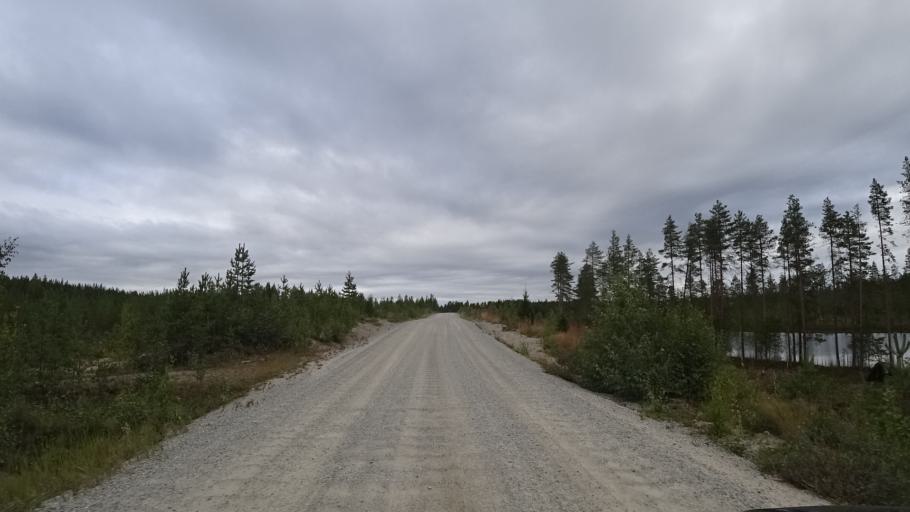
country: FI
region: North Karelia
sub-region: Pielisen Karjala
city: Lieksa
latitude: 63.2506
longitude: 30.3317
